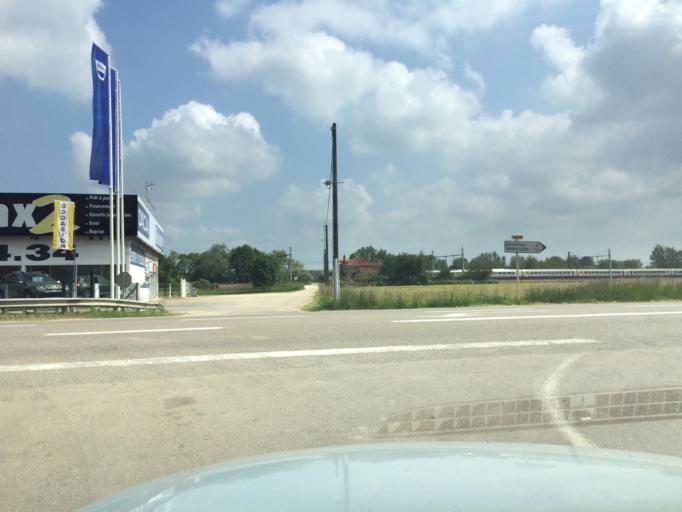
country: FR
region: Bourgogne
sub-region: Departement de l'Yonne
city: Laroche-Saint-Cydroine
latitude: 47.9567
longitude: 3.4490
